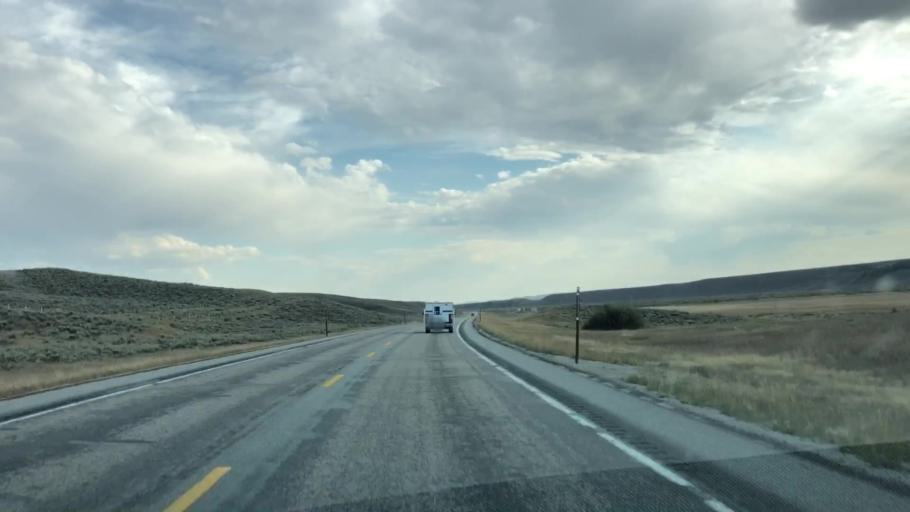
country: US
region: Wyoming
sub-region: Sublette County
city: Pinedale
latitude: 43.0832
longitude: -110.1624
